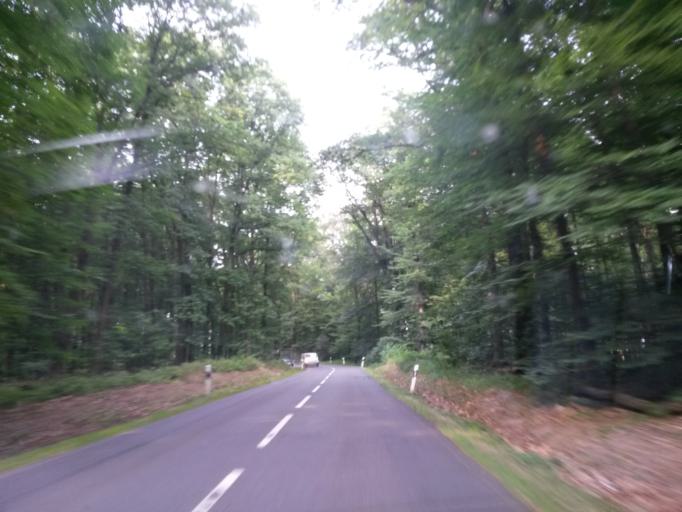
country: DE
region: North Rhine-Westphalia
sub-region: Regierungsbezirk Koln
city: Hennef
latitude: 50.7882
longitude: 7.3019
